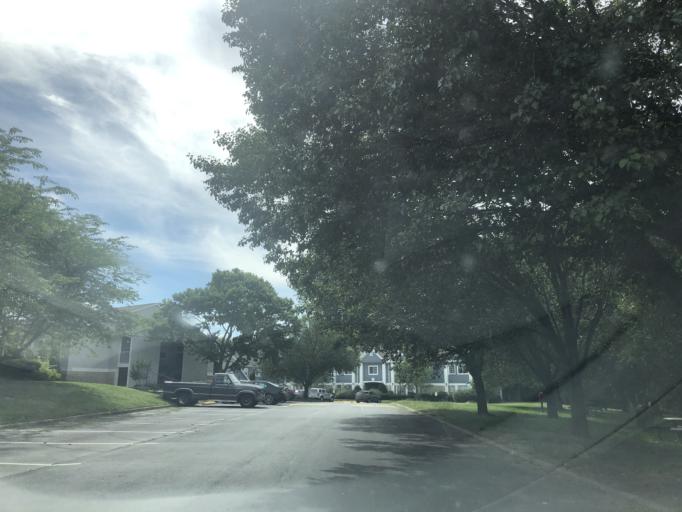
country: US
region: Tennessee
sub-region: Davidson County
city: Belle Meade
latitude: 36.0747
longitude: -86.9430
